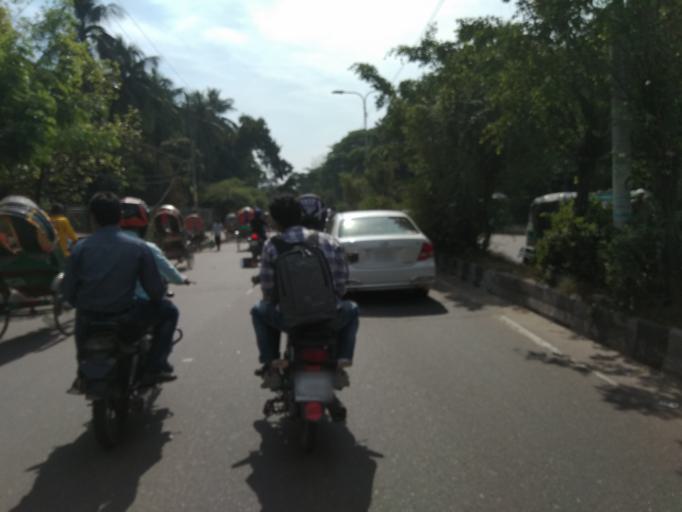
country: BD
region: Dhaka
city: Azimpur
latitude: 23.7354
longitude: 90.3956
